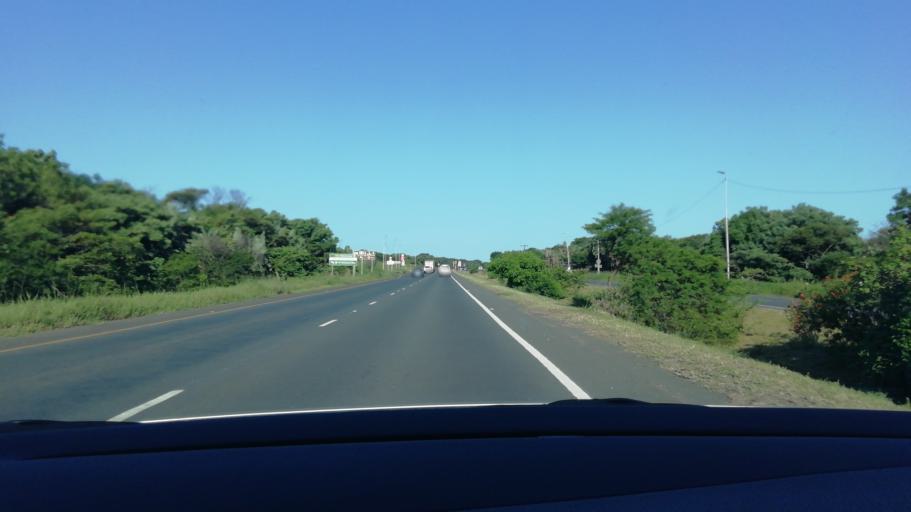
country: ZA
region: KwaZulu-Natal
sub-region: uThungulu District Municipality
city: Richards Bay
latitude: -28.7685
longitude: 32.0462
